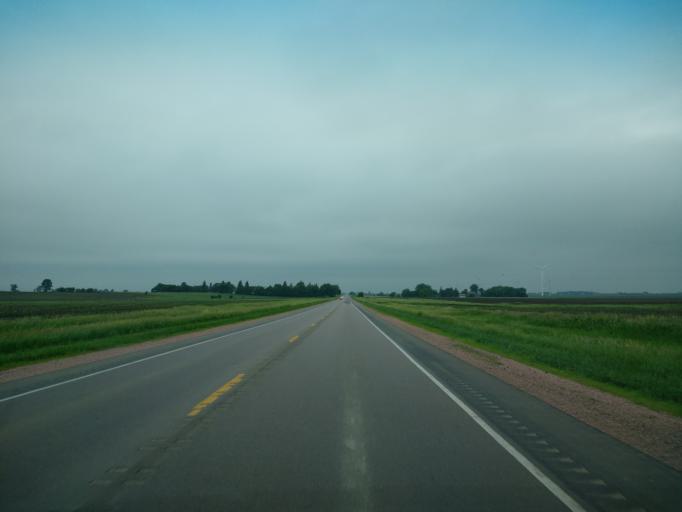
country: US
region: Iowa
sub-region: O'Brien County
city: Sanborn
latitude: 43.1861
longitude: -95.6711
